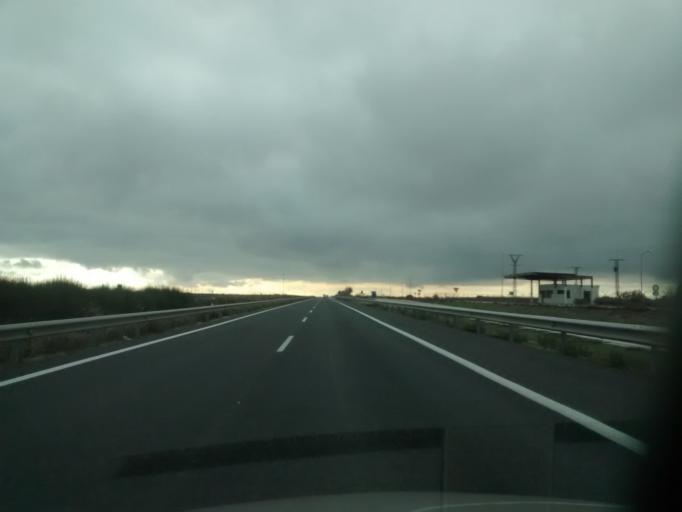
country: ES
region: Castille-La Mancha
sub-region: Provincia de Guadalajara
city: Valdearenas
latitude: 40.7947
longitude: -2.9640
